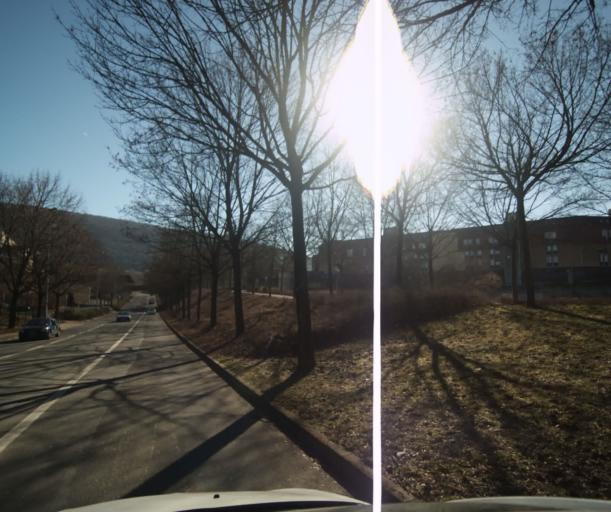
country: FR
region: Franche-Comte
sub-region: Departement du Doubs
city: Avanne-Aveney
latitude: 47.2188
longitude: 5.9759
